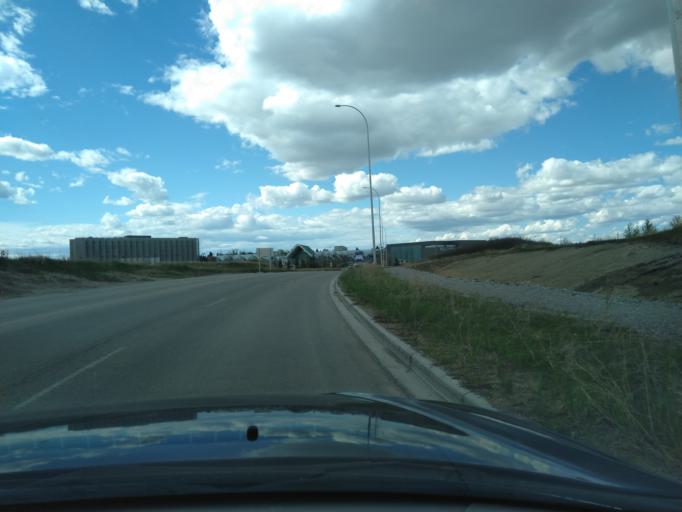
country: CA
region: Alberta
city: Calgary
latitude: 51.0042
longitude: -114.1443
